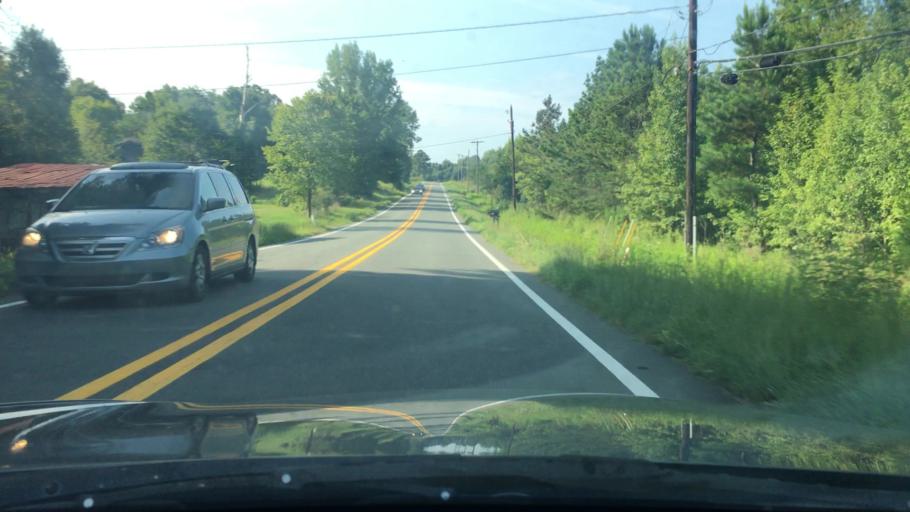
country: US
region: North Carolina
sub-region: Alamance County
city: Green Level
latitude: 36.2345
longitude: -79.3224
